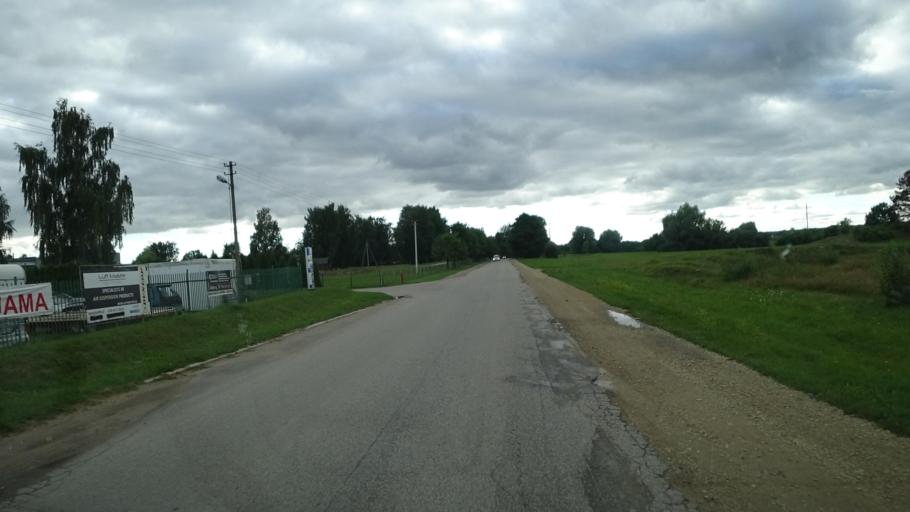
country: LT
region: Marijampoles apskritis
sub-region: Marijampole Municipality
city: Marijampole
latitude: 54.5816
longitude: 23.3710
